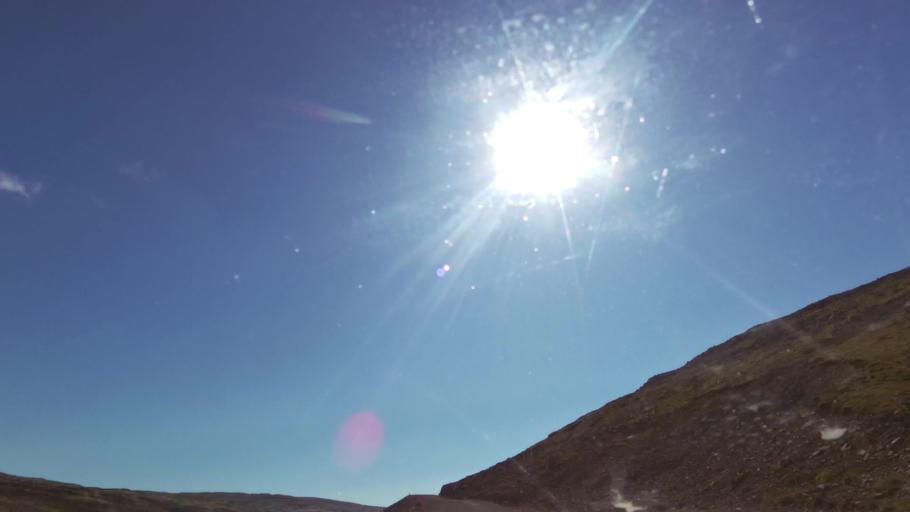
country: IS
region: West
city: Olafsvik
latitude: 65.5626
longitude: -24.1798
